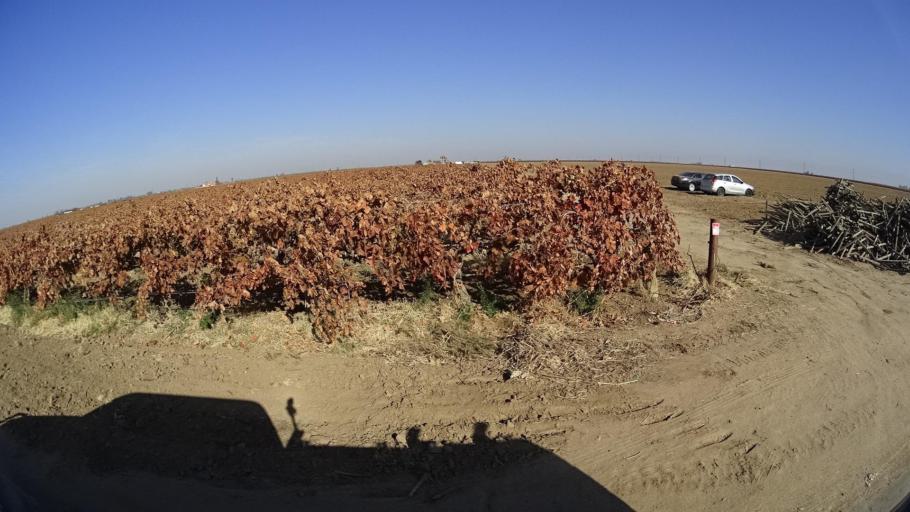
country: US
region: California
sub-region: Kern County
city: Delano
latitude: 35.7324
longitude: -119.2095
